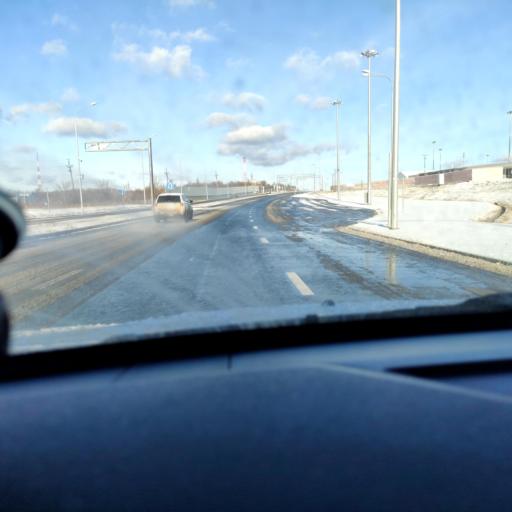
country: RU
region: Samara
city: Samara
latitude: 53.2761
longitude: 50.2318
